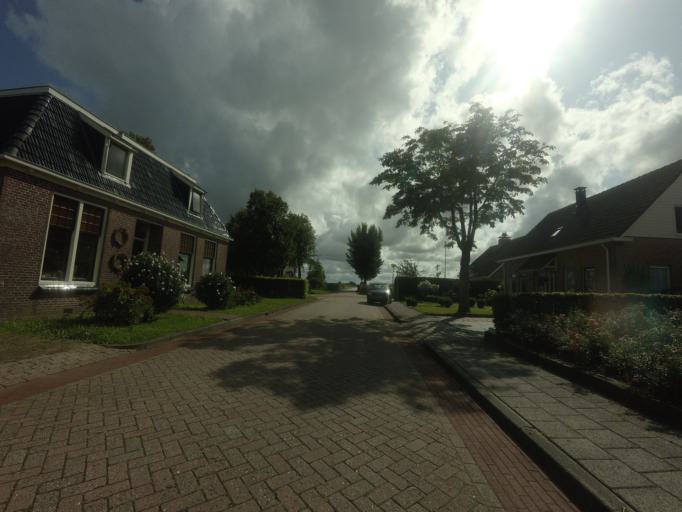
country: NL
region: Friesland
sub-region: Sudwest Fryslan
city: Scharnegoutum
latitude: 53.0757
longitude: 5.6364
